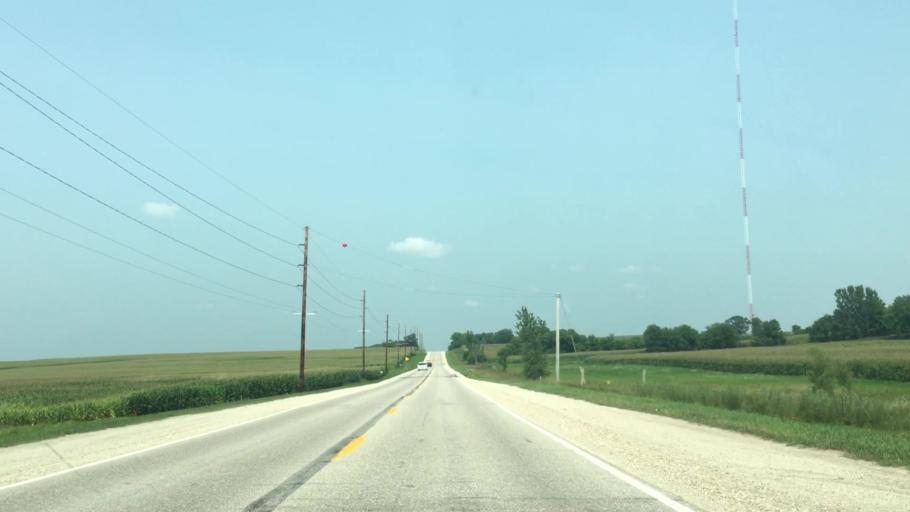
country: US
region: Iowa
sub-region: Benton County
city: Urbana
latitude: 42.2879
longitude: -91.8900
